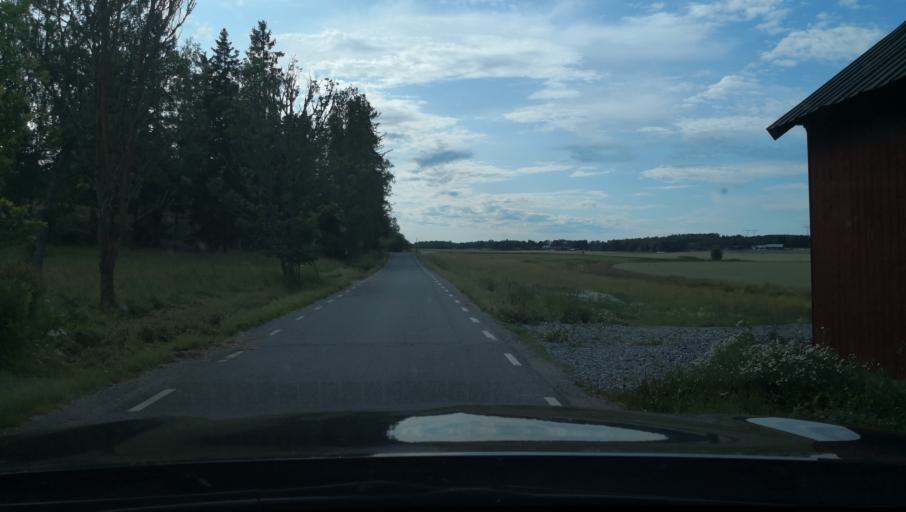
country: SE
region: Uppsala
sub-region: Enkopings Kommun
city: Orsundsbro
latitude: 59.6909
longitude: 17.3611
